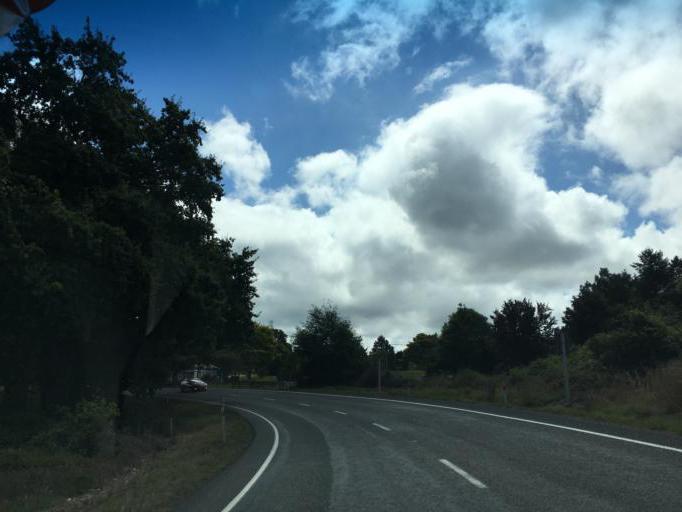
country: NZ
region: Hawke's Bay
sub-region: Wairoa District
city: Wairoa
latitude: -39.0628
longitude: 177.0371
